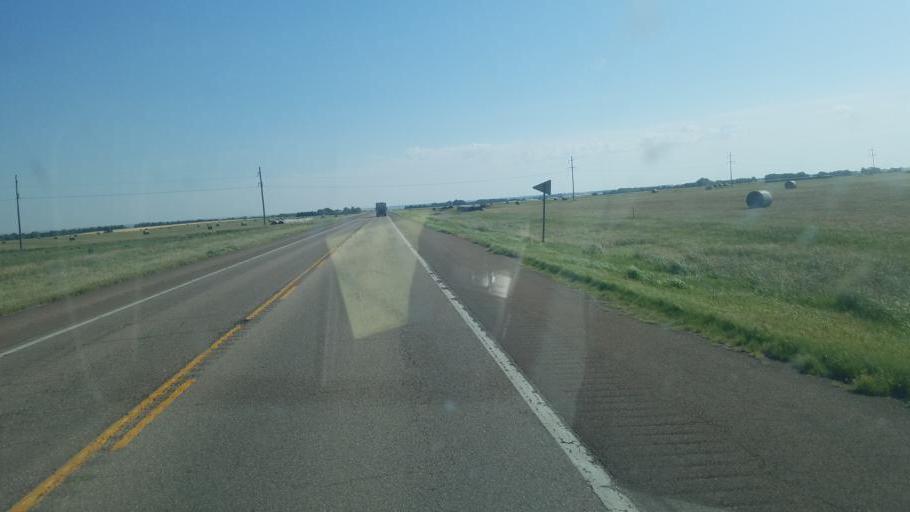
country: US
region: Kansas
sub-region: Barton County
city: Great Bend
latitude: 38.3893
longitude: -98.6777
